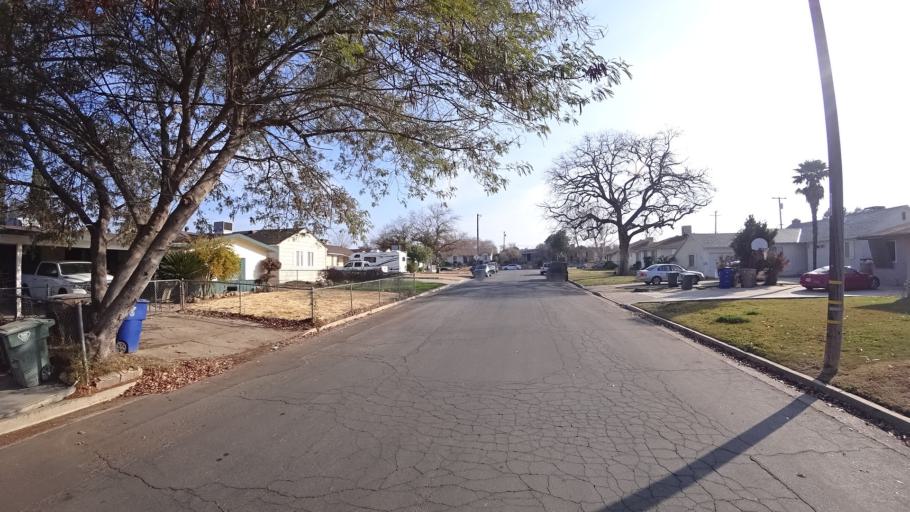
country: US
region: California
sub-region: Kern County
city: Oildale
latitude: 35.4010
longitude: -118.9839
